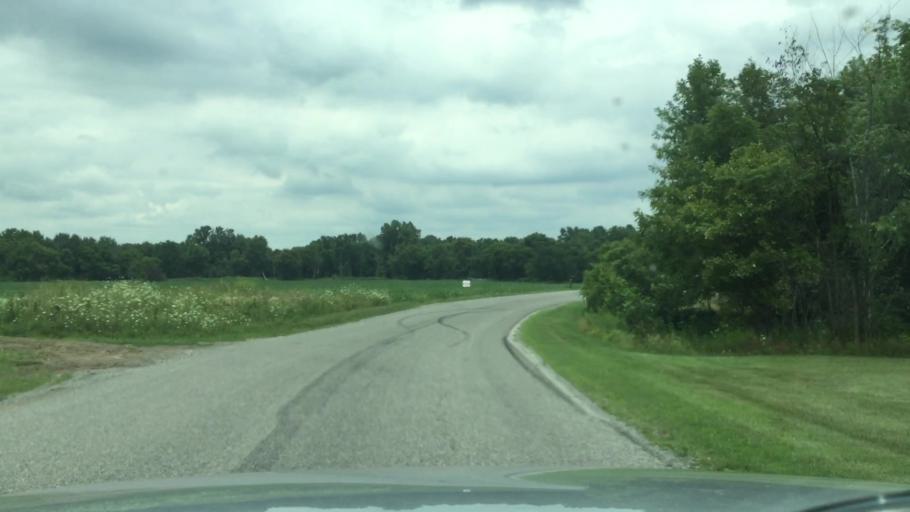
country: US
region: Michigan
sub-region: Saginaw County
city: Burt
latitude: 43.2743
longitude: -83.8858
